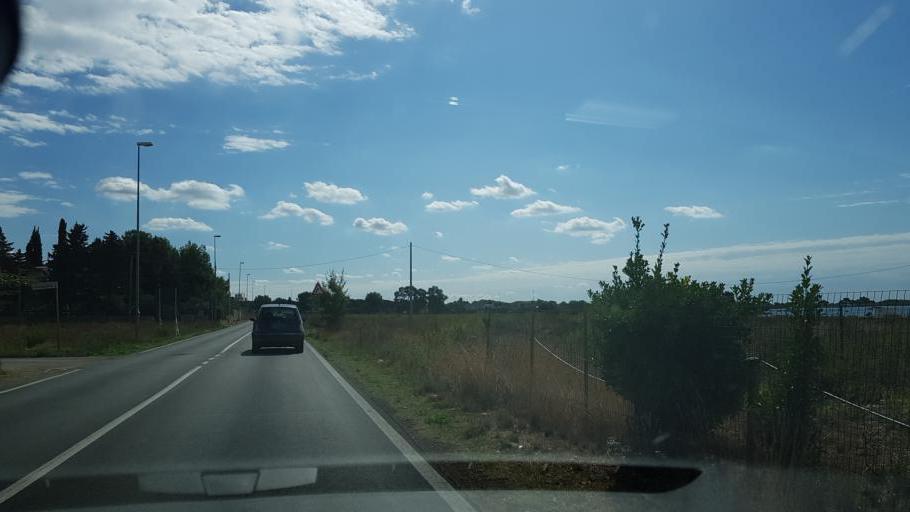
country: IT
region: Apulia
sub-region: Provincia di Lecce
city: Porto Cesareo
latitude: 40.2521
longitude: 17.9089
